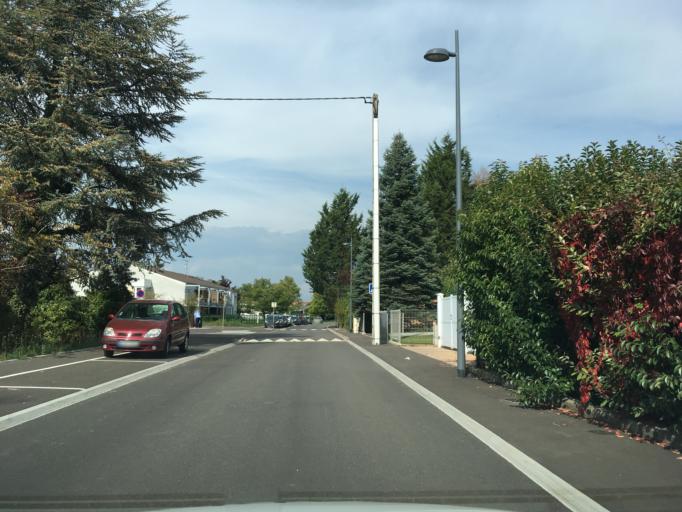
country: FR
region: Alsace
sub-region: Departement du Haut-Rhin
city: Colmar
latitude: 48.0592
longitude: 7.3611
